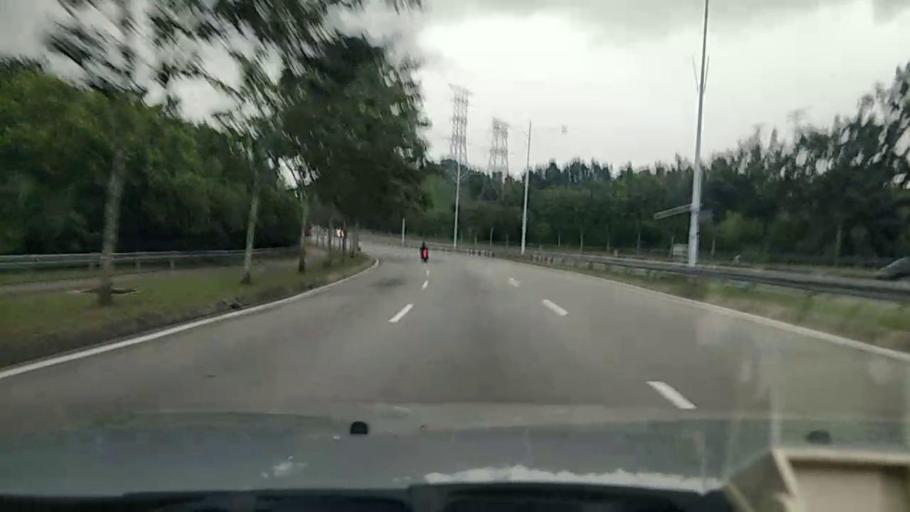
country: MY
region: Putrajaya
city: Putrajaya
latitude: 2.9524
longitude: 101.7142
